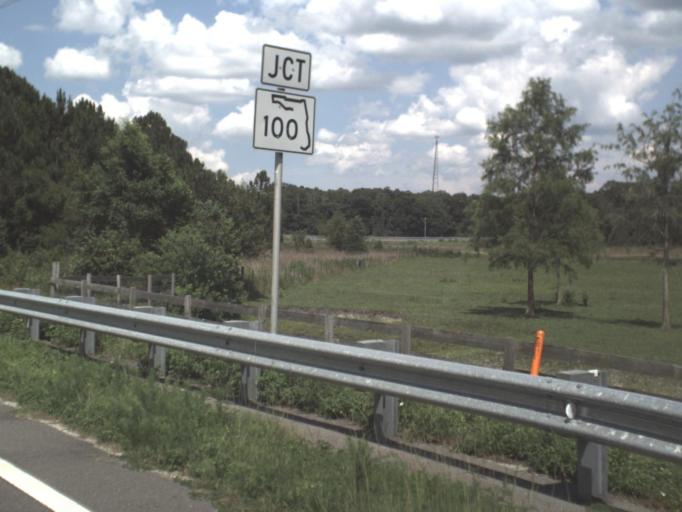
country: US
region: Florida
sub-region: Clay County
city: Keystone Heights
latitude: 29.7367
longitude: -81.9647
